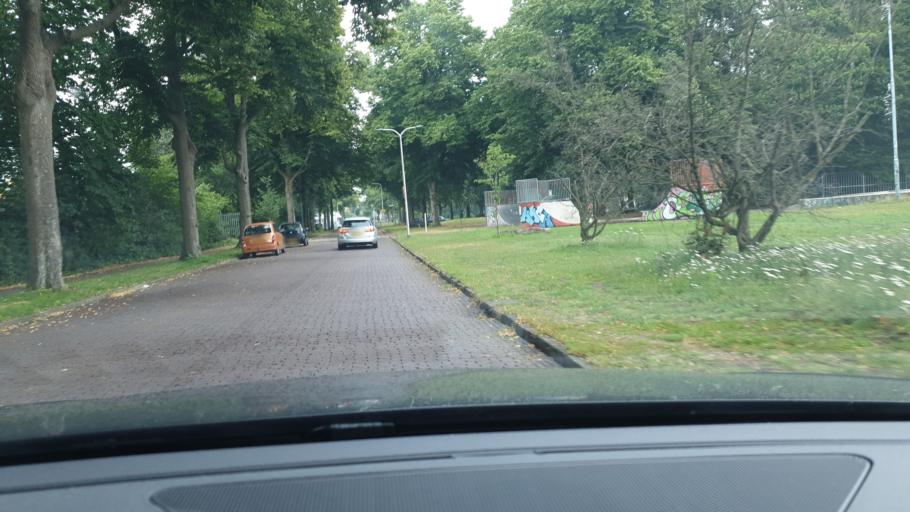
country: NL
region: Gelderland
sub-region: Gemeente Nijmegen
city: Nijmegen
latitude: 51.8283
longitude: 5.8368
